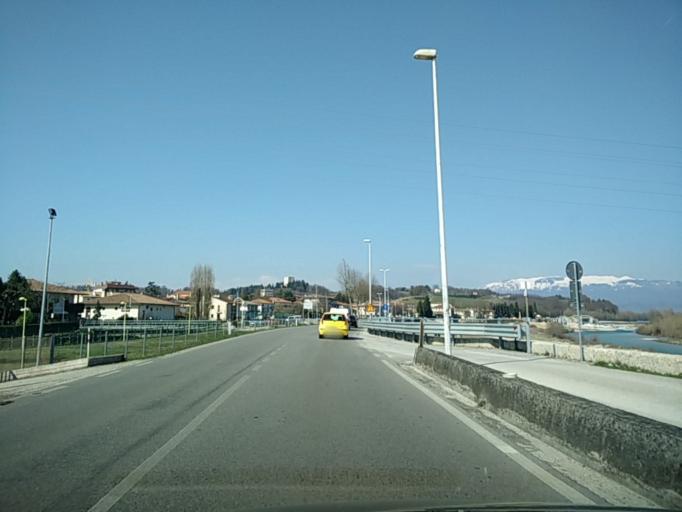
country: IT
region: Veneto
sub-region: Provincia di Treviso
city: Nervesa della Battaglia
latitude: 45.8241
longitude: 12.2160
